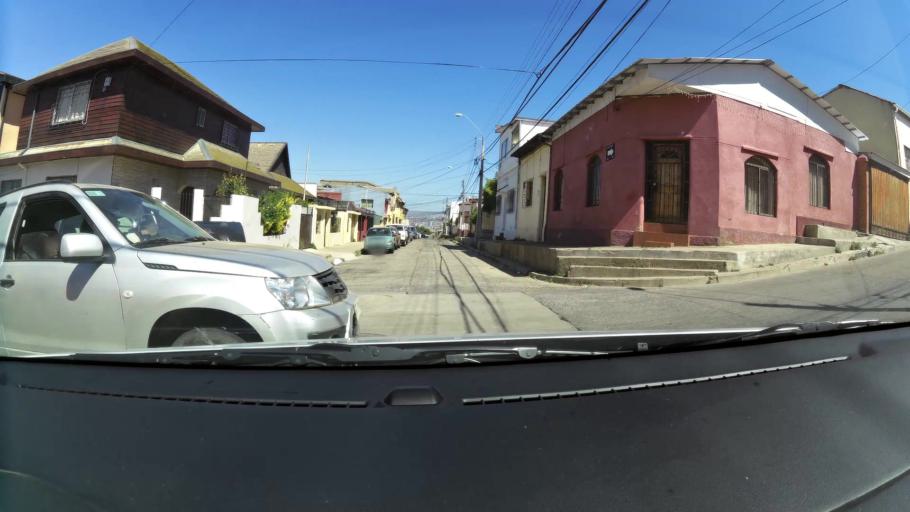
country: CL
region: Valparaiso
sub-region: Provincia de Valparaiso
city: Valparaiso
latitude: -33.0318
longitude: -71.6407
